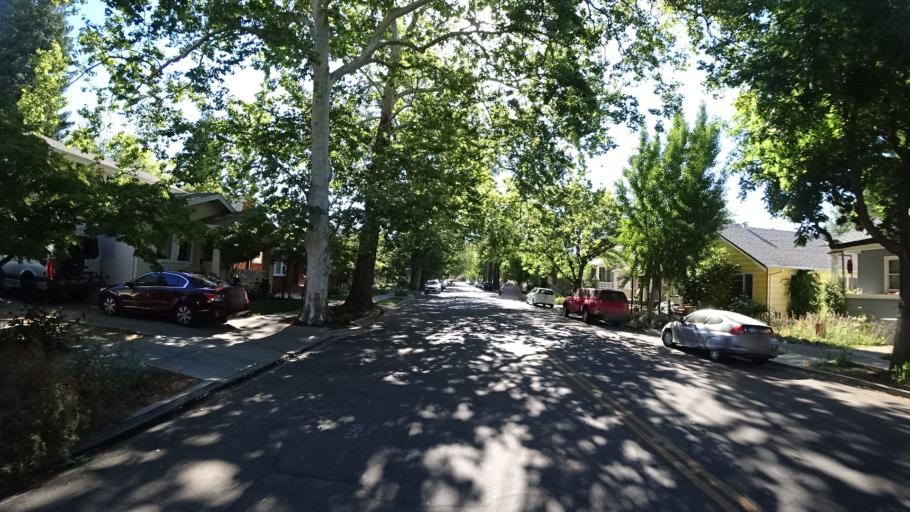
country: US
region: California
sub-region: Sacramento County
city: Sacramento
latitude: 38.5510
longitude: -121.4784
